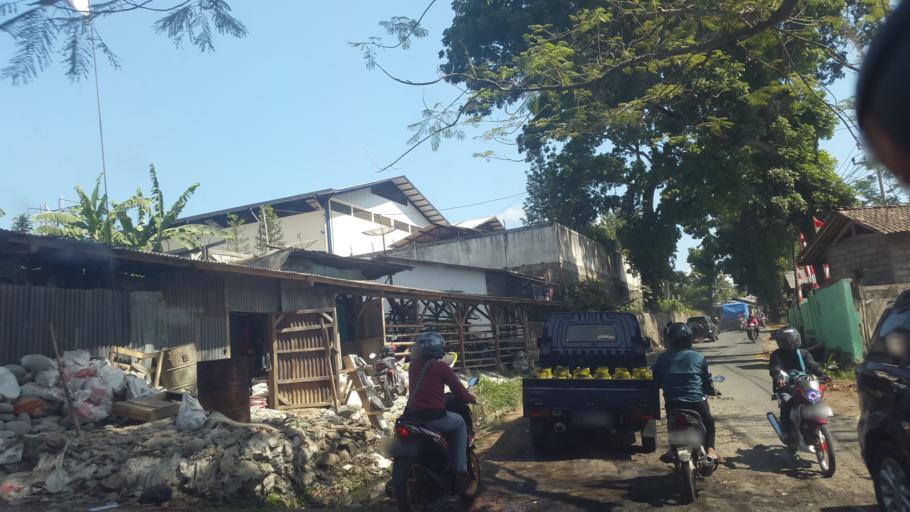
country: ID
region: West Java
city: Suryabakti
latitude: -6.9819
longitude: 106.8496
